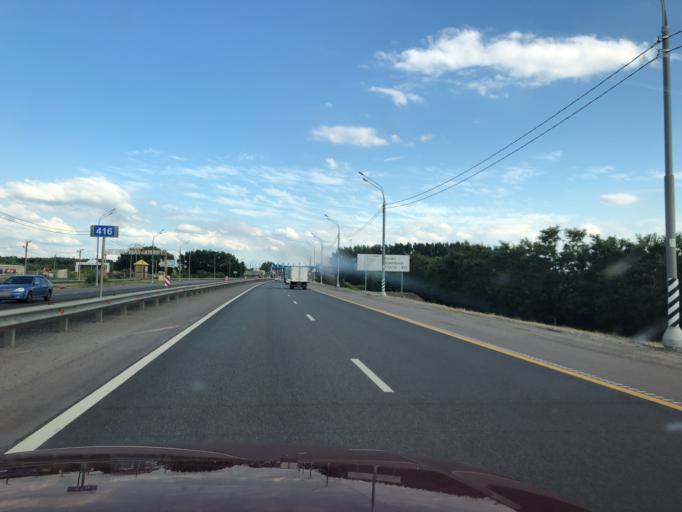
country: RU
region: Lipetsk
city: Zadonsk
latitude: 52.4340
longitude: 38.8189
